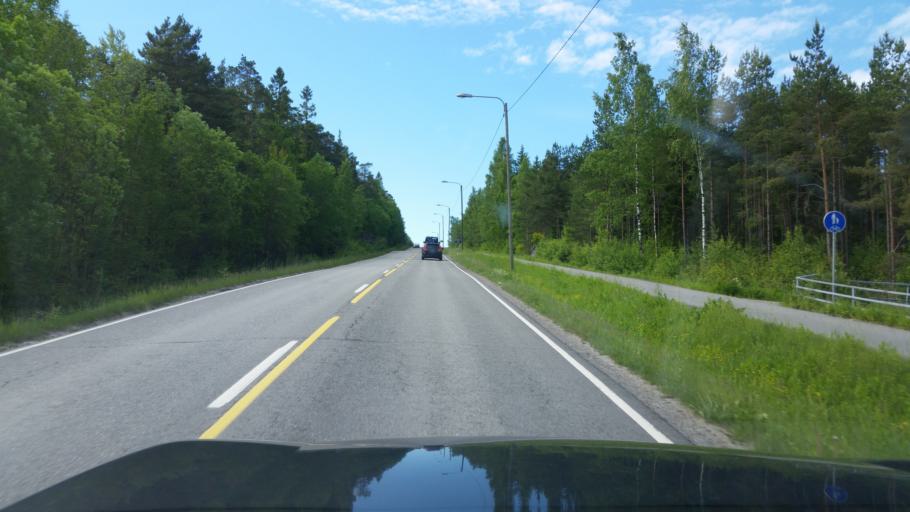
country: FI
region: Varsinais-Suomi
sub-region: Aboland-Turunmaa
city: Laensi-Turunmaa
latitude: 60.2926
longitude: 22.2658
